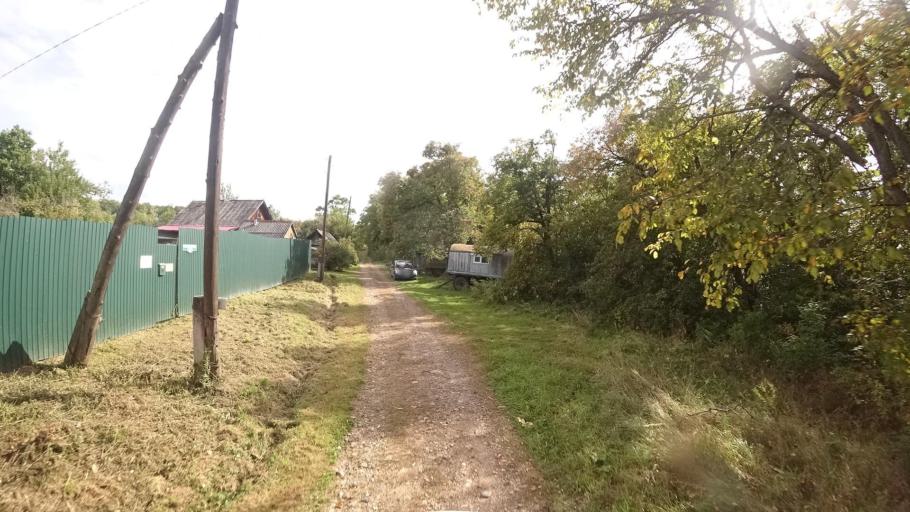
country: RU
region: Primorskiy
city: Dostoyevka
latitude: 44.3242
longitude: 133.4848
